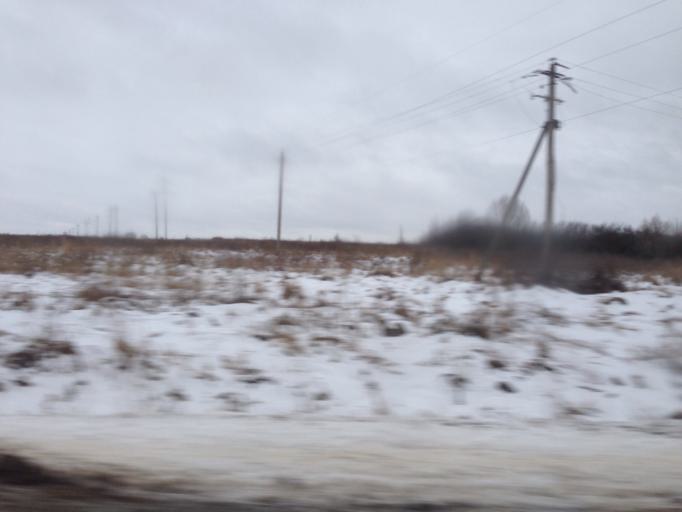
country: RU
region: Tula
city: Kamenetskiy
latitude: 53.9997
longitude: 38.2002
